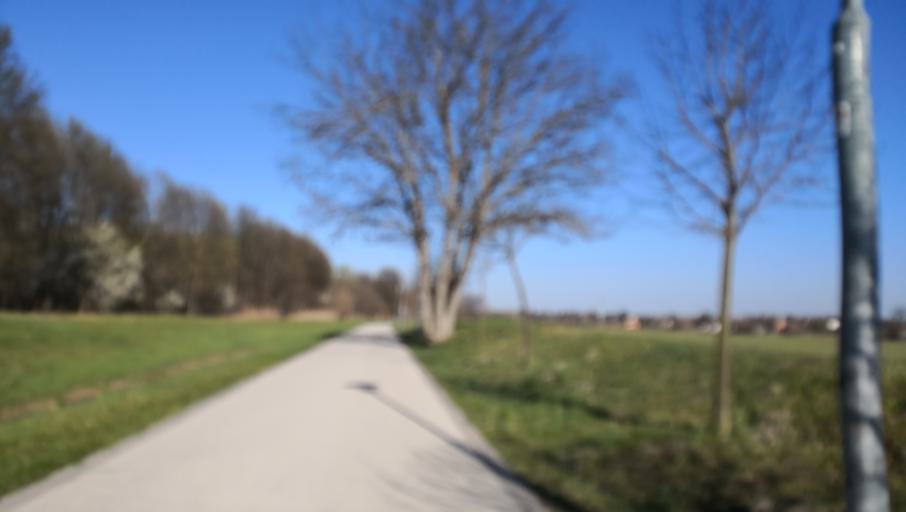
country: HU
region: Budapest
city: Budapest XVII. keruelet
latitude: 47.4841
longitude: 19.2596
